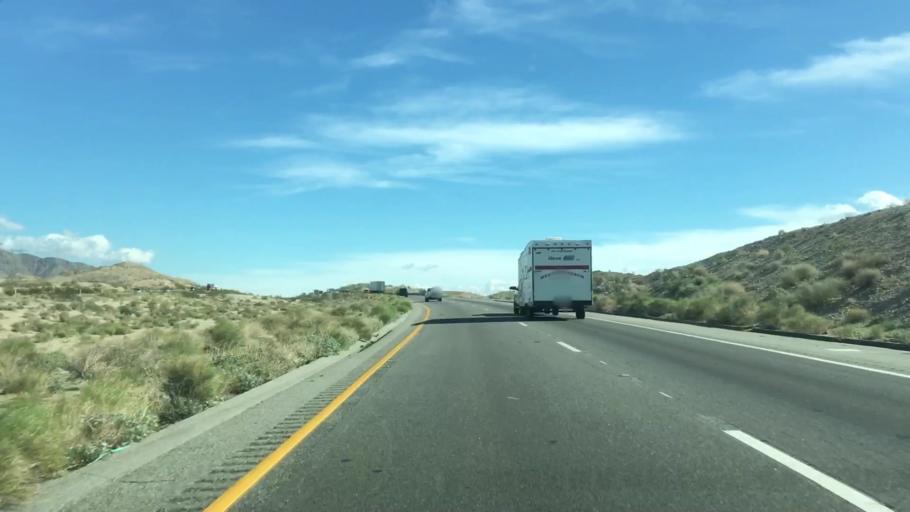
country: US
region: California
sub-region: Riverside County
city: Mecca
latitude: 33.6792
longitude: -115.9960
